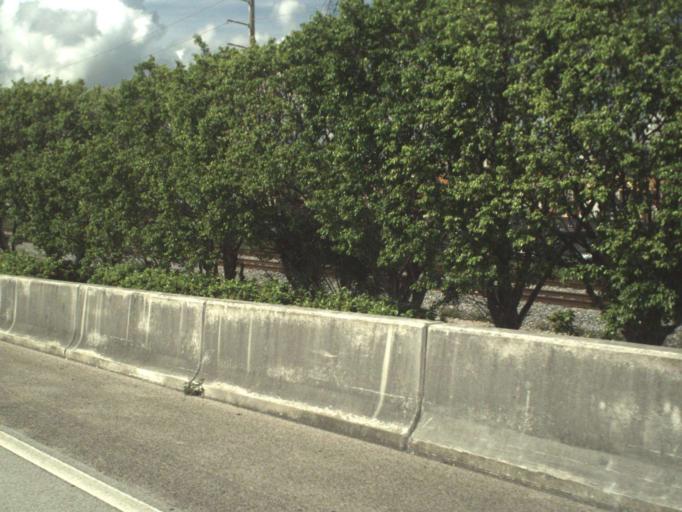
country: US
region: Florida
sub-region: Miami-Dade County
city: Aventura
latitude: 25.9612
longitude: -80.1472
